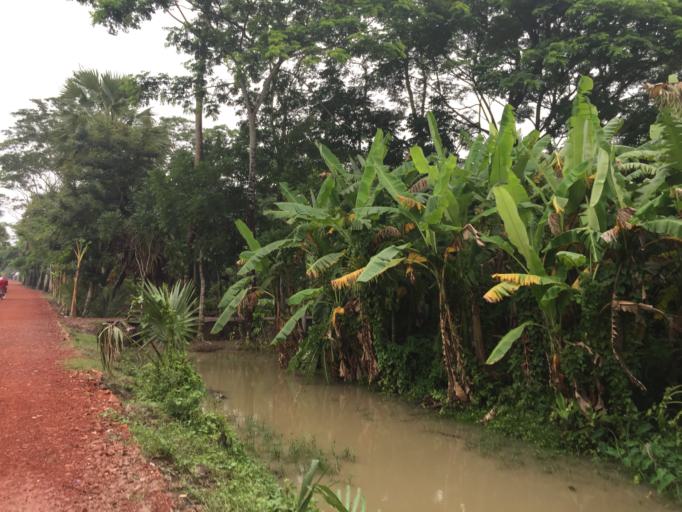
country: BD
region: Barisal
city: Mathba
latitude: 22.2056
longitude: 89.9375
